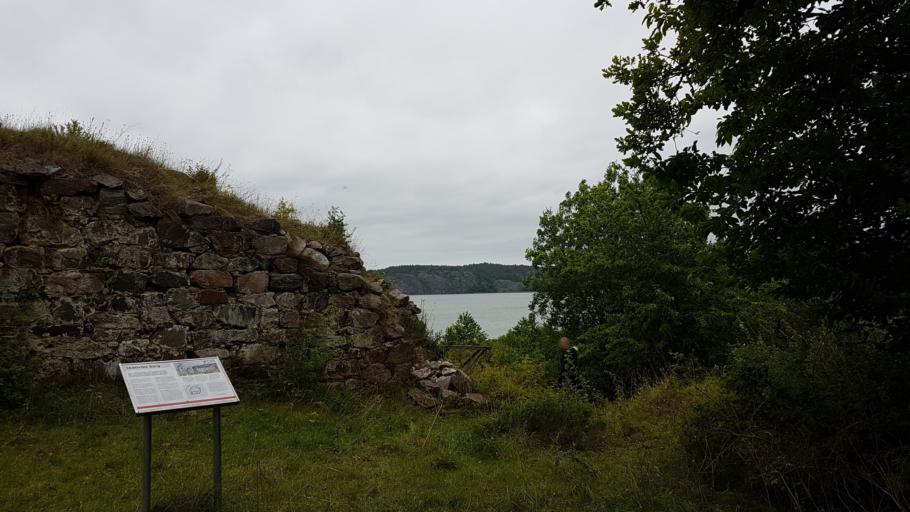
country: SE
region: OEstergoetland
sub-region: Valdemarsviks Kommun
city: Gusum
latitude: 58.4319
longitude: 16.5695
